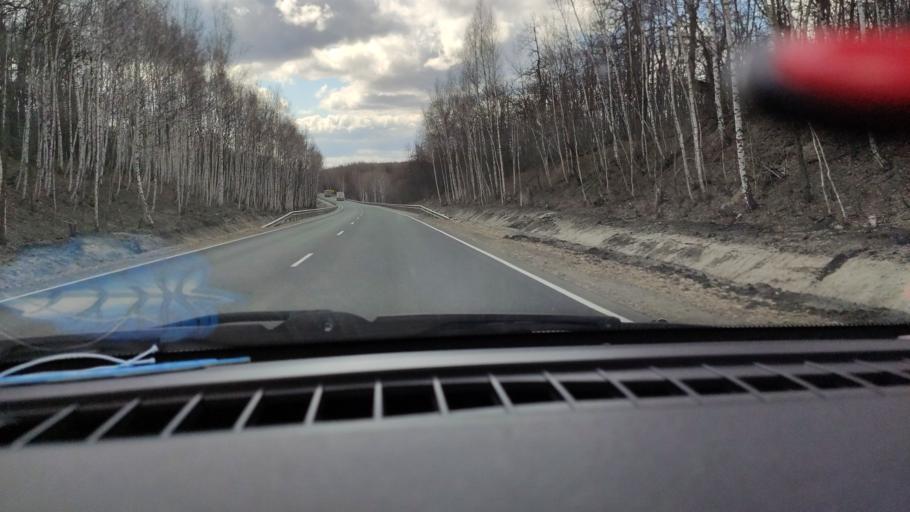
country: RU
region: Saratov
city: Khvalynsk
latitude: 52.4406
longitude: 48.0095
